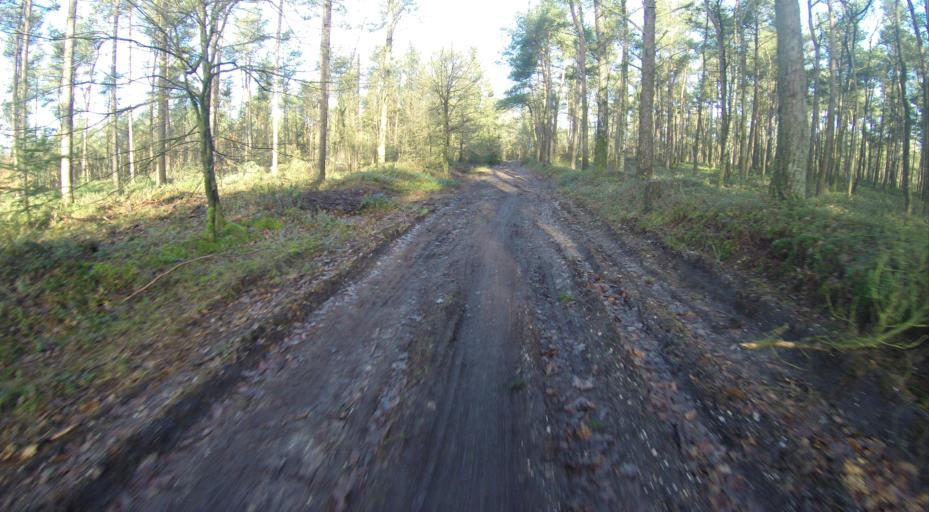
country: NL
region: Overijssel
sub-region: Gemeente Hof van Twente
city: Markelo
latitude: 52.3251
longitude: 6.4221
